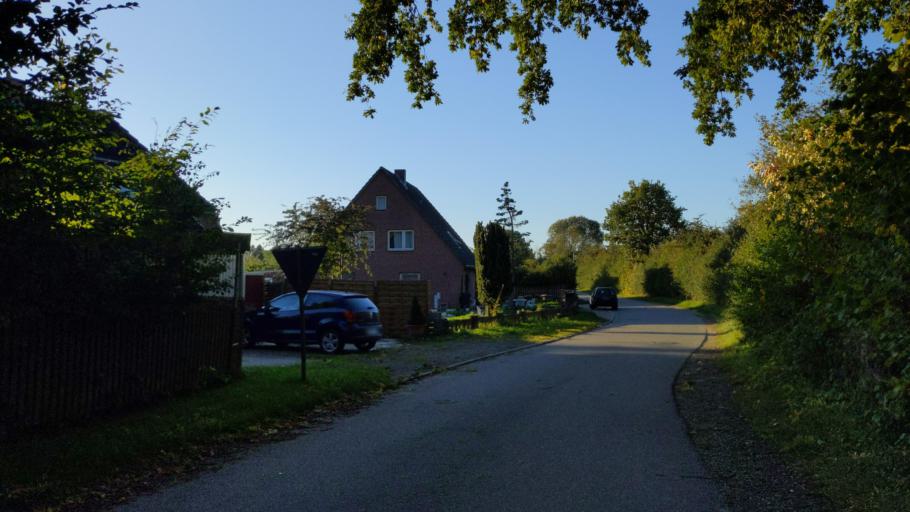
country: DE
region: Schleswig-Holstein
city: Ahrensbok
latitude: 54.0323
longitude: 10.6072
